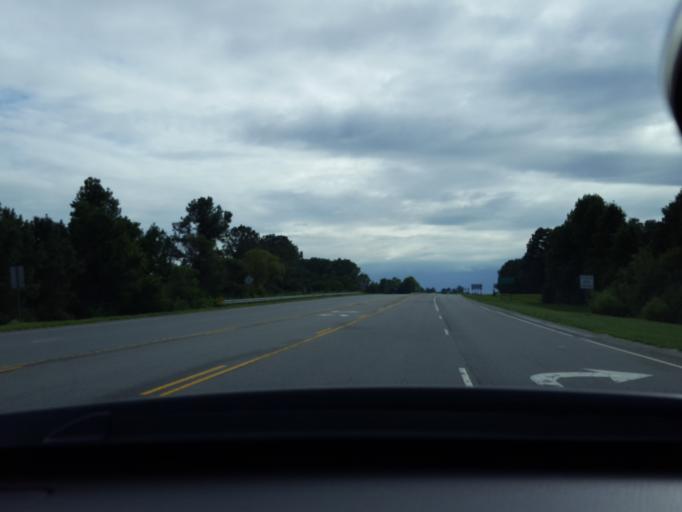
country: US
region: North Carolina
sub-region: Duplin County
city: Kenansville
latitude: 34.9199
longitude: -78.0217
